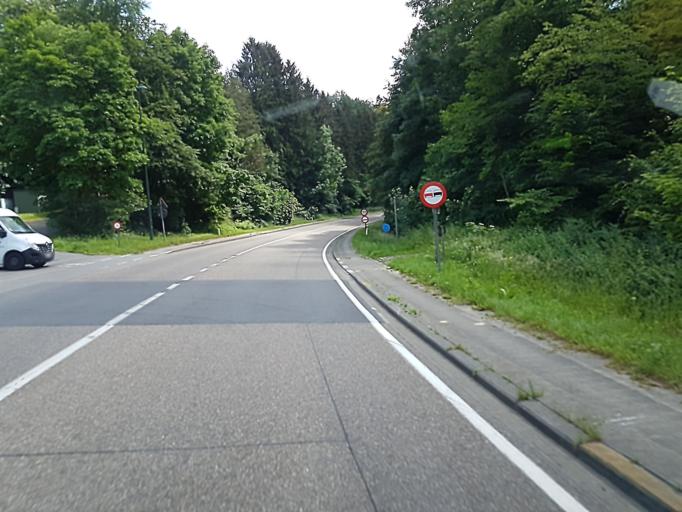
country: BE
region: Flanders
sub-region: Provincie Vlaams-Brabant
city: Hoeilaart
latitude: 50.7638
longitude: 4.4511
